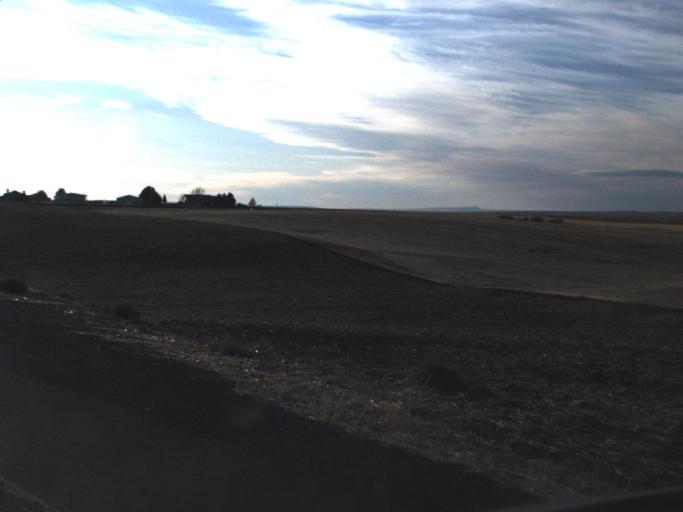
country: US
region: Washington
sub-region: Walla Walla County
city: Walla Walla East
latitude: 46.1086
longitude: -118.2323
